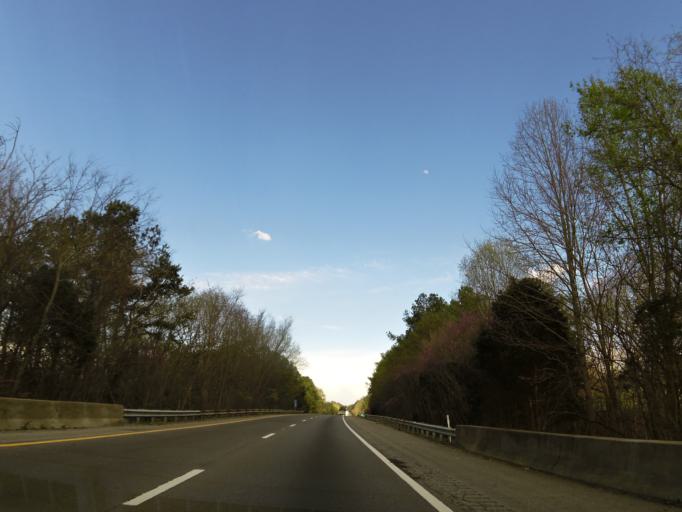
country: US
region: Tennessee
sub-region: Dickson County
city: Dickson
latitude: 36.0070
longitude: -87.4046
